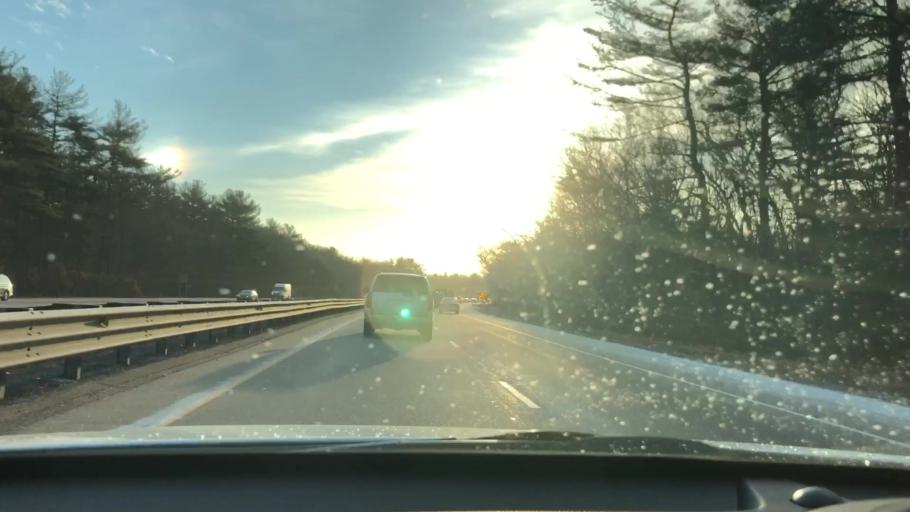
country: US
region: Massachusetts
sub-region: Norfolk County
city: Weymouth
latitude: 42.1829
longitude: -70.9224
